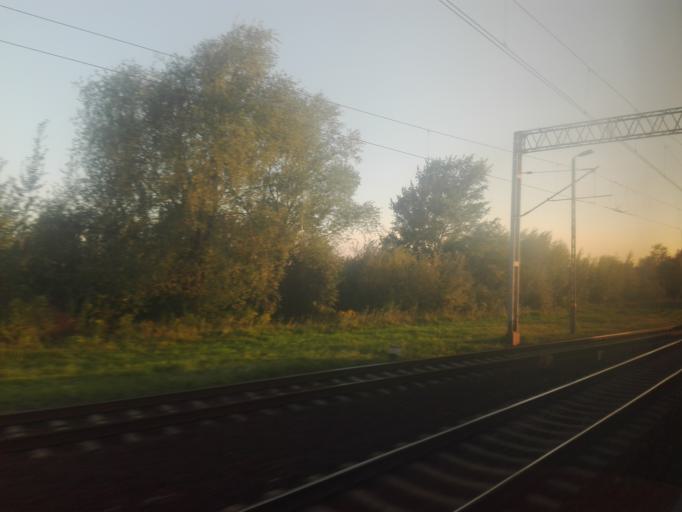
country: PL
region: Masovian Voivodeship
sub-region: Powiat warszawski zachodni
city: Blonie
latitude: 52.1865
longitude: 20.5979
